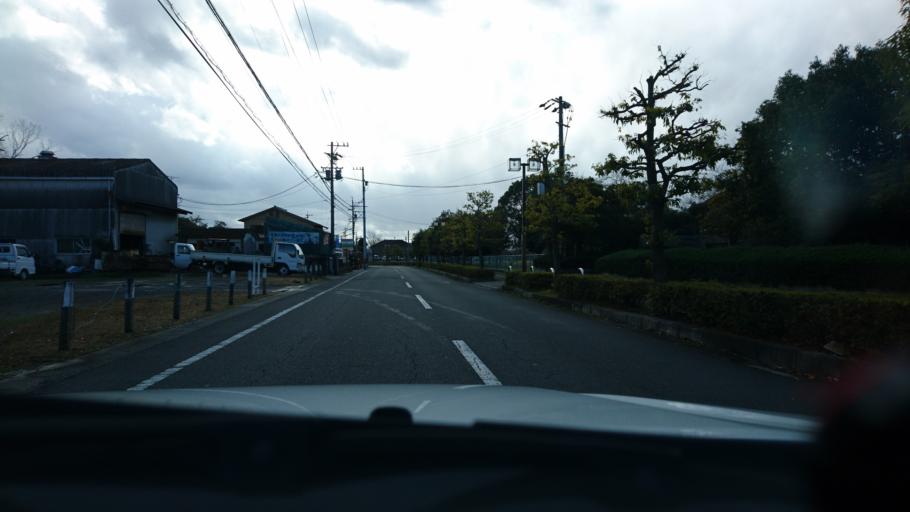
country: JP
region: Mie
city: Ueno-ebisumachi
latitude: 34.7580
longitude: 136.1563
